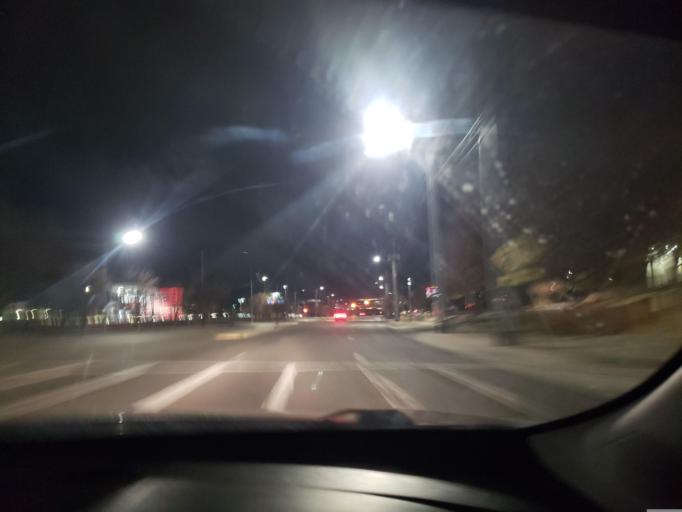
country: US
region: New Mexico
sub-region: Bernalillo County
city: Albuquerque
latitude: 35.0686
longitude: -106.6286
